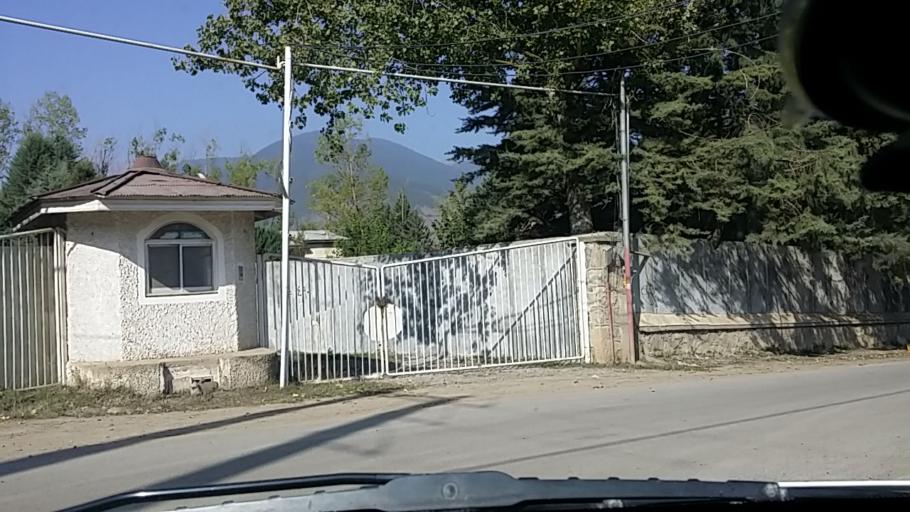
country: IR
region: Mazandaran
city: `Abbasabad
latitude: 36.5023
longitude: 51.1734
